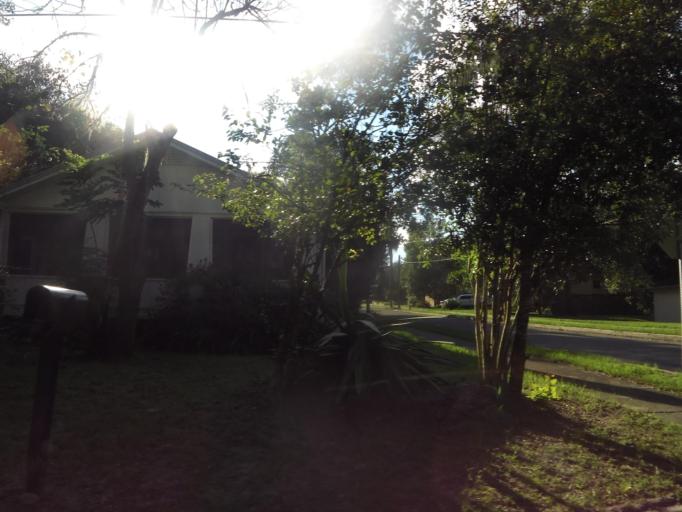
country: US
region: Florida
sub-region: Putnam County
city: Palatka
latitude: 29.6400
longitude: -81.6444
